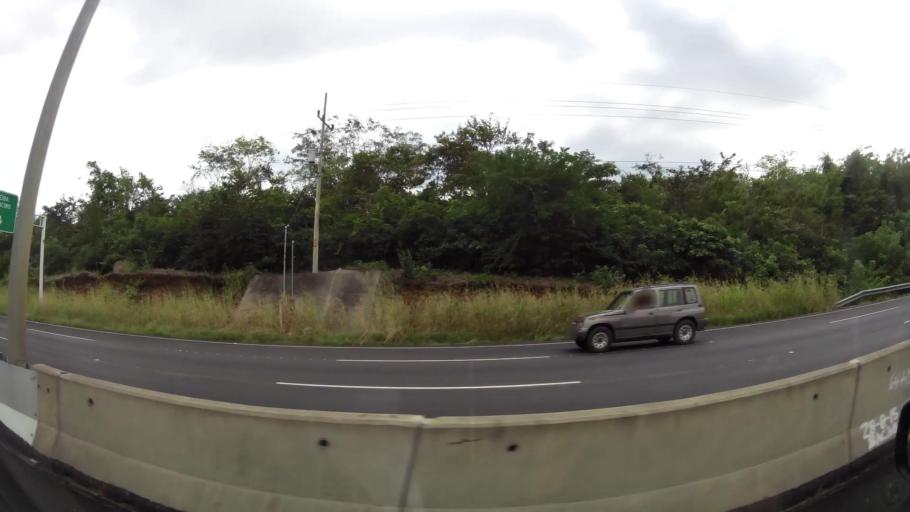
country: CR
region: Alajuela
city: Orotina
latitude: 9.8926
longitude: -84.6142
